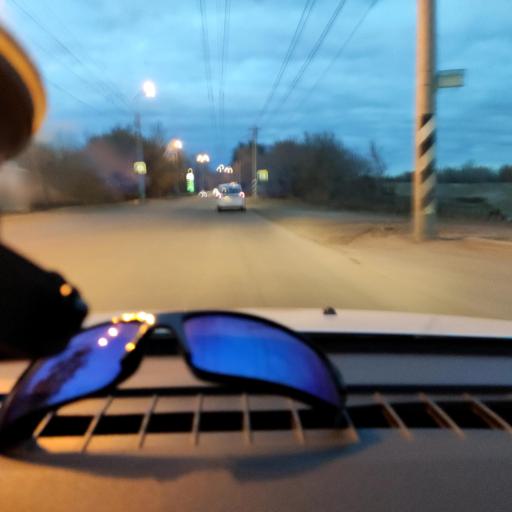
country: RU
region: Samara
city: Samara
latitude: 53.1470
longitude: 50.0955
